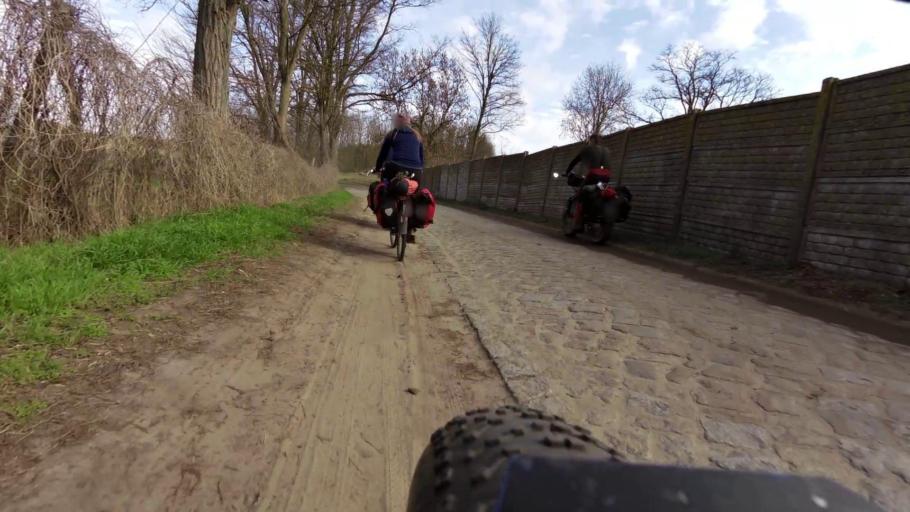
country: DE
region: Brandenburg
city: Brieskow-Finkenheerd
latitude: 52.2850
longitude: 14.6178
